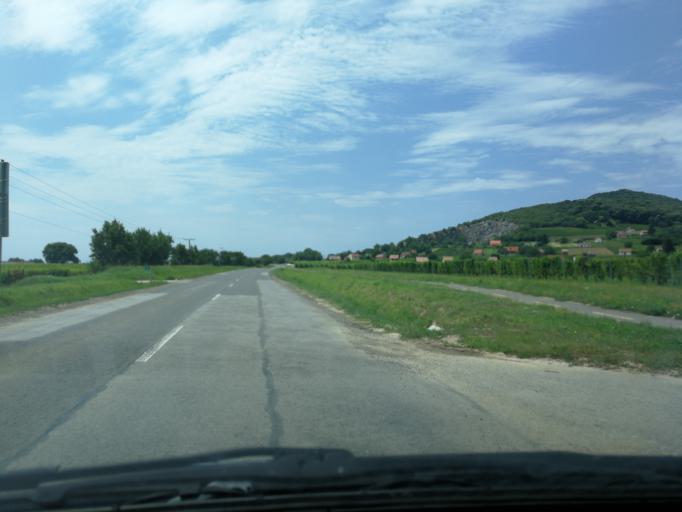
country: HU
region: Baranya
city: Villany
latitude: 45.8588
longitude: 18.4385
